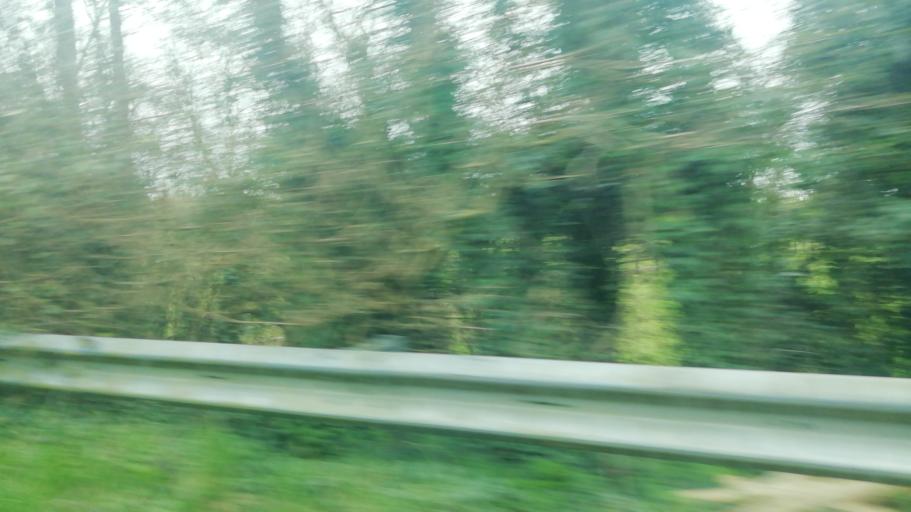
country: IE
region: Leinster
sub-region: Kildare
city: Celbridge
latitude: 53.3635
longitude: -6.5661
